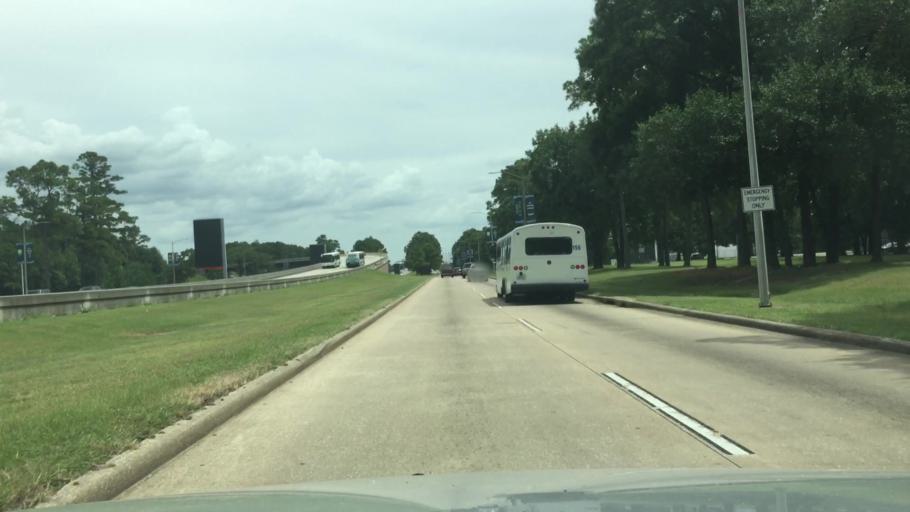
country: US
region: Texas
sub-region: Harris County
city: Aldine
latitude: 29.9726
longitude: -95.3407
